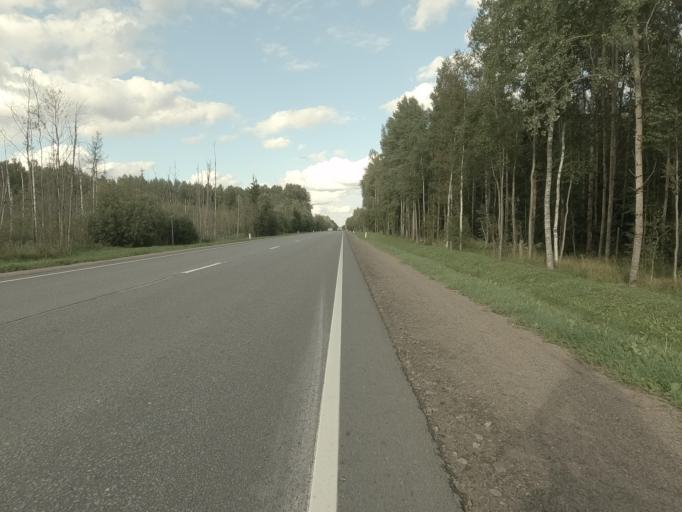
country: RU
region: Leningrad
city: Mga
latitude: 59.6837
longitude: 30.9568
